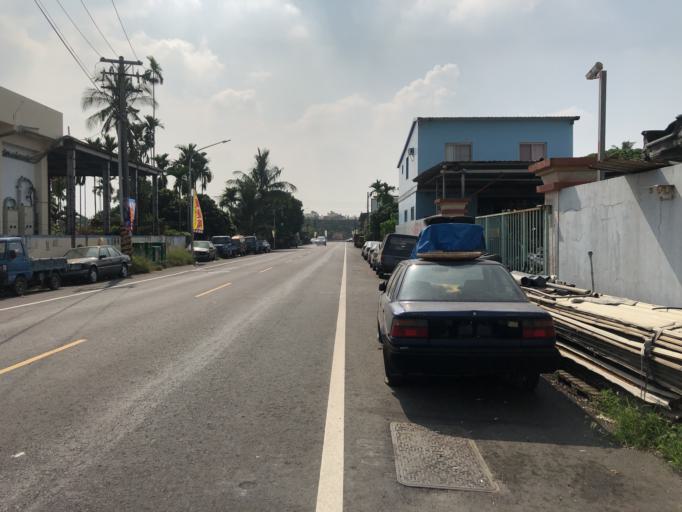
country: TW
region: Taiwan
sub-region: Pingtung
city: Pingtung
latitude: 22.5492
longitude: 120.5340
